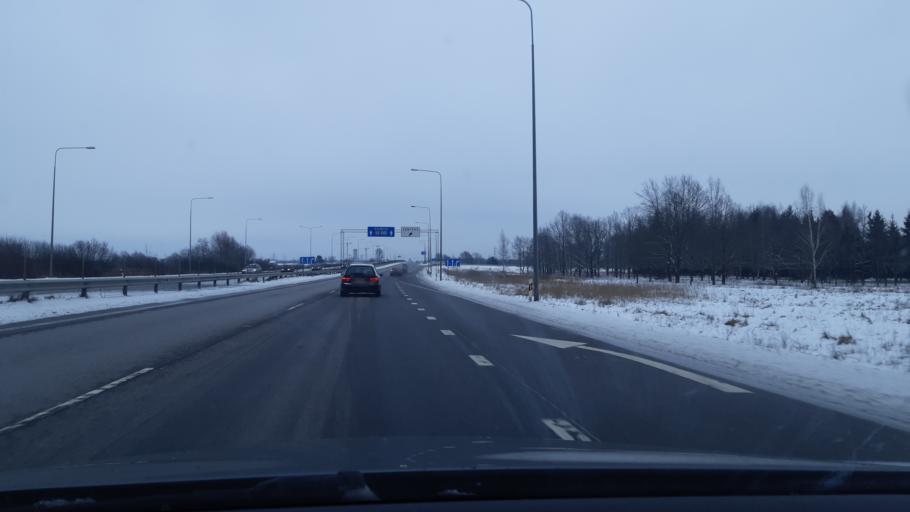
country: LT
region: Kauno apskritis
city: Dainava (Kaunas)
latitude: 54.9342
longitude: 23.9715
